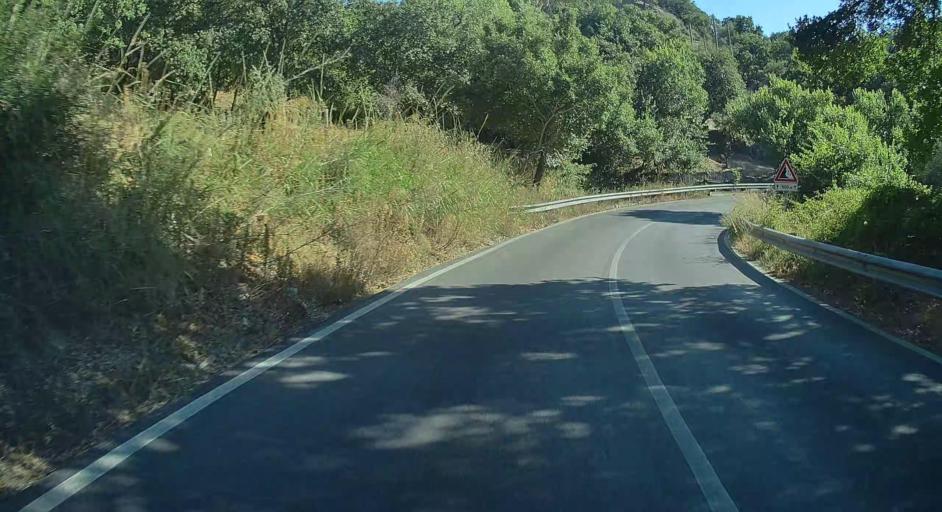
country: IT
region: Sicily
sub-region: Messina
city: Oliveri
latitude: 38.1360
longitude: 15.0349
